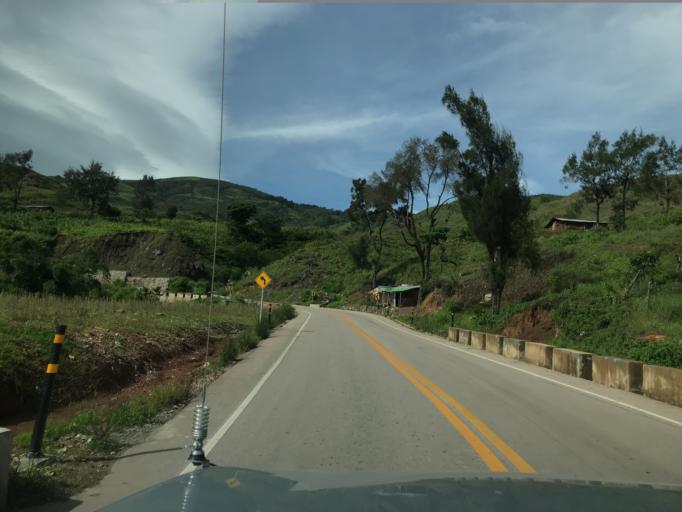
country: TL
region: Aileu
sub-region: Aileu Villa
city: Aileu
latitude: -8.8097
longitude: 125.5967
